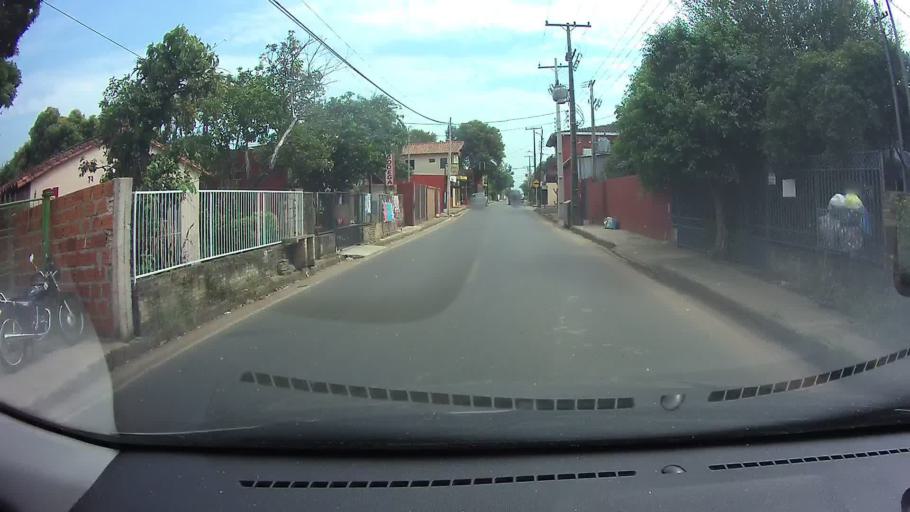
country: PY
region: Central
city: San Lorenzo
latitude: -25.2901
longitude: -57.5046
